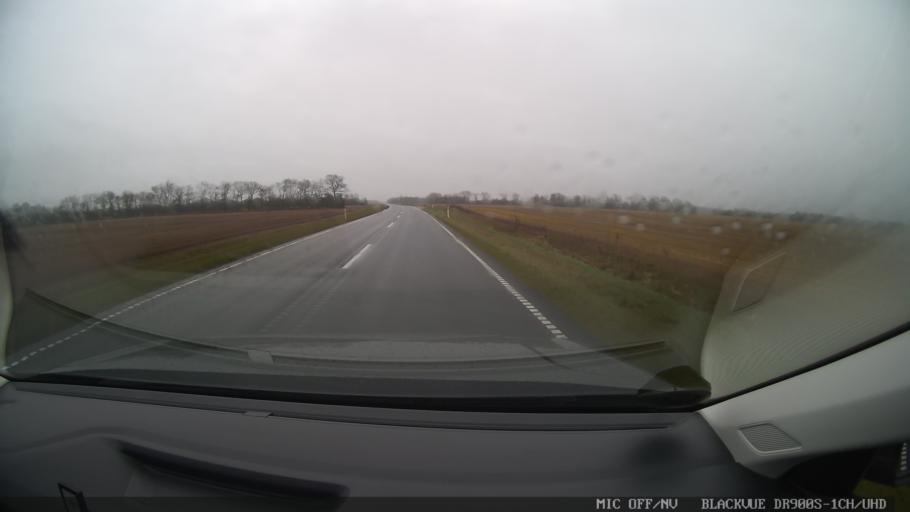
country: DK
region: Central Jutland
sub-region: Herning Kommune
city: Sunds
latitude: 56.2789
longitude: 8.9519
